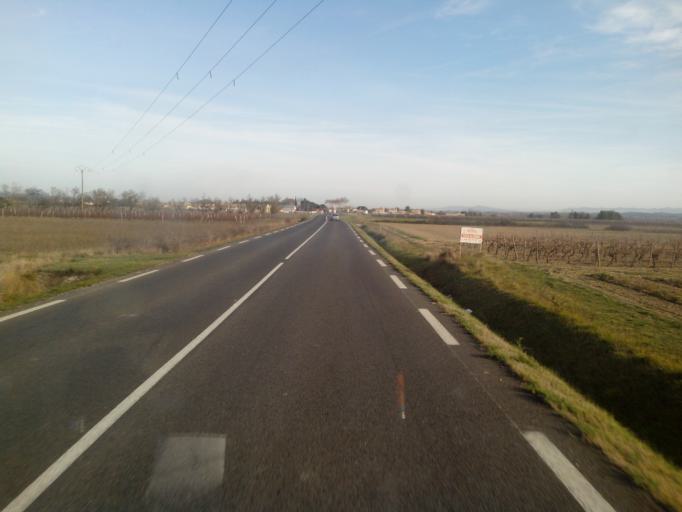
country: FR
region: Languedoc-Roussillon
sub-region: Departement de l'Aude
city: Alzonne
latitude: 43.2553
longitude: 2.1614
